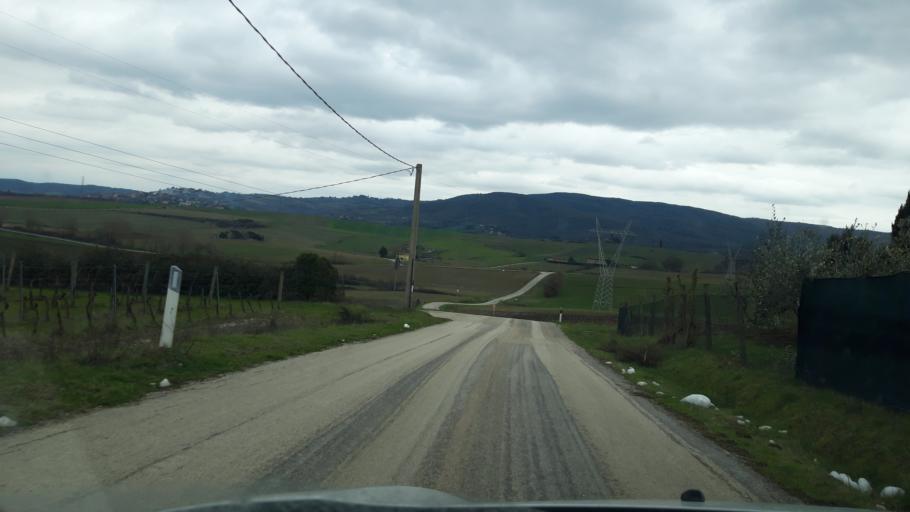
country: IT
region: Umbria
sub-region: Provincia di Perugia
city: Tavernelle
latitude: 42.9896
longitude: 12.1740
